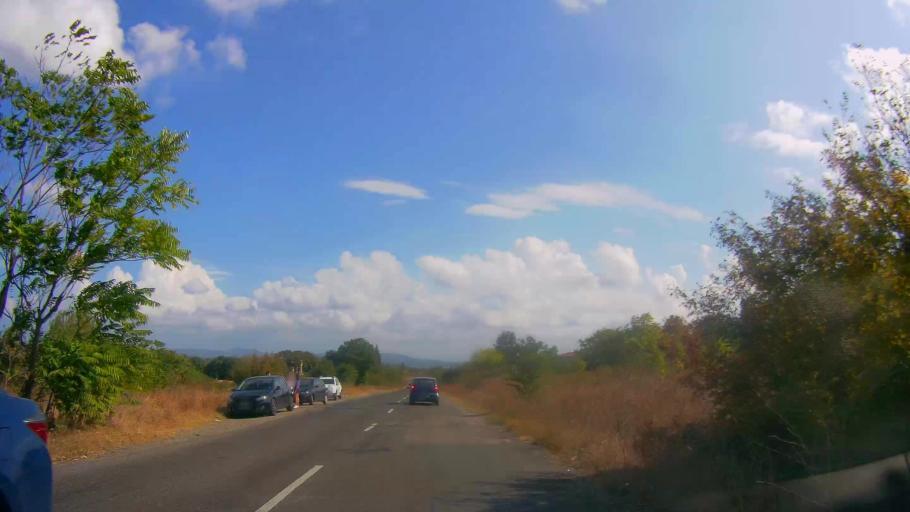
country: BG
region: Burgas
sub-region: Obshtina Burgas
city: Burgas
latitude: 42.4759
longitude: 27.4158
